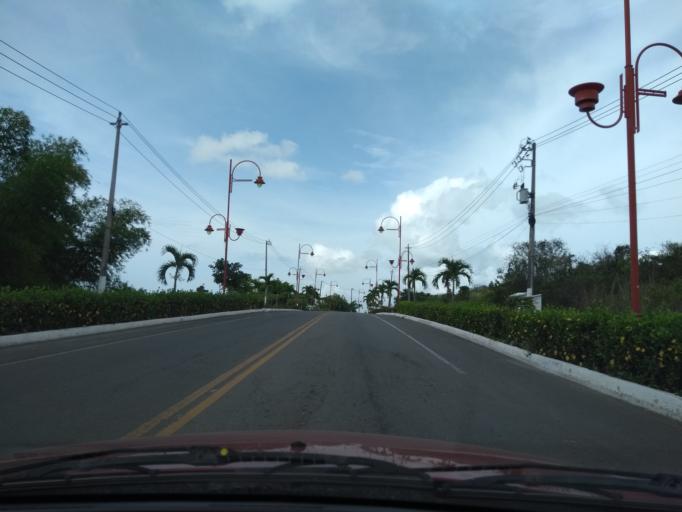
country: BR
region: Bahia
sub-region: Sao Francisco Do Conde
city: Sao Francisco do Conde
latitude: -12.6140
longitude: -38.6562
